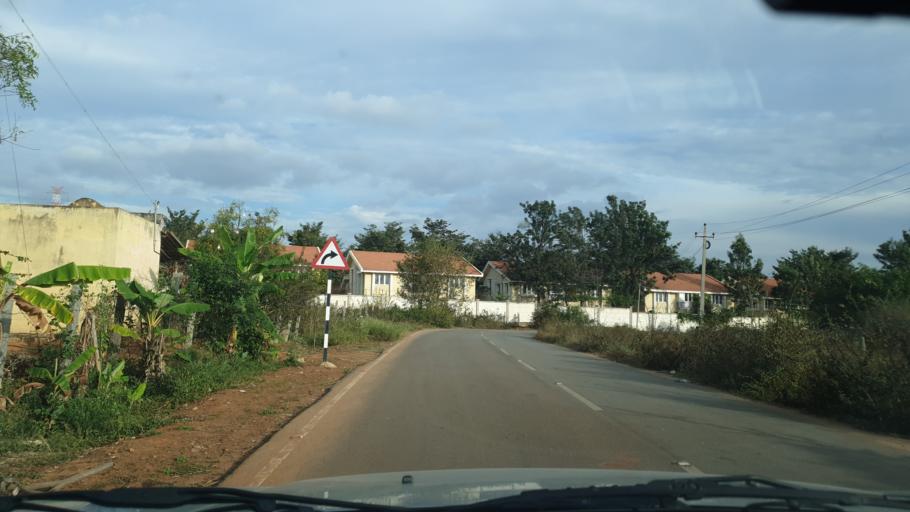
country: IN
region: Karnataka
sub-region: Bangalore Urban
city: Yelahanka
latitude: 13.1936
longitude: 77.6226
